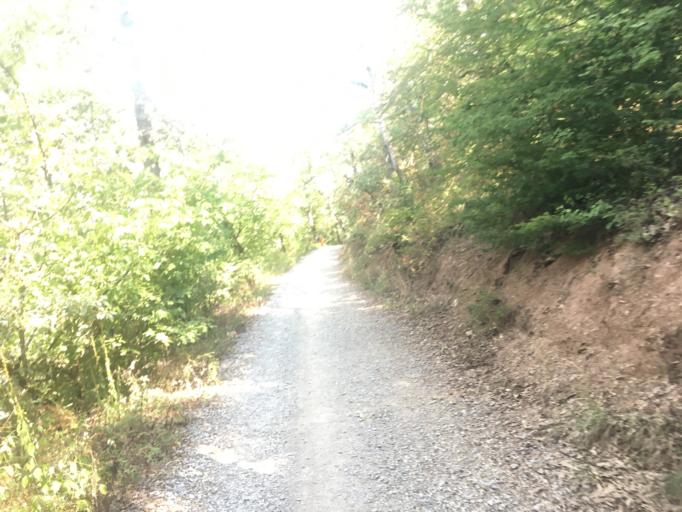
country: XK
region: Pristina
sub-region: Komuna e Prishtines
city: Pristina
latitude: 42.6640
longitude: 21.2233
